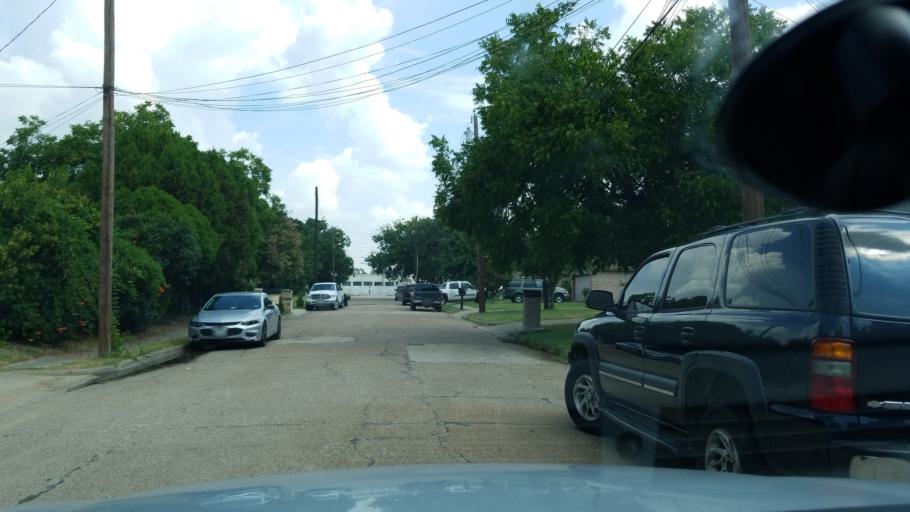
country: US
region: Texas
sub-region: Dallas County
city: Irving
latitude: 32.8327
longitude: -96.9204
